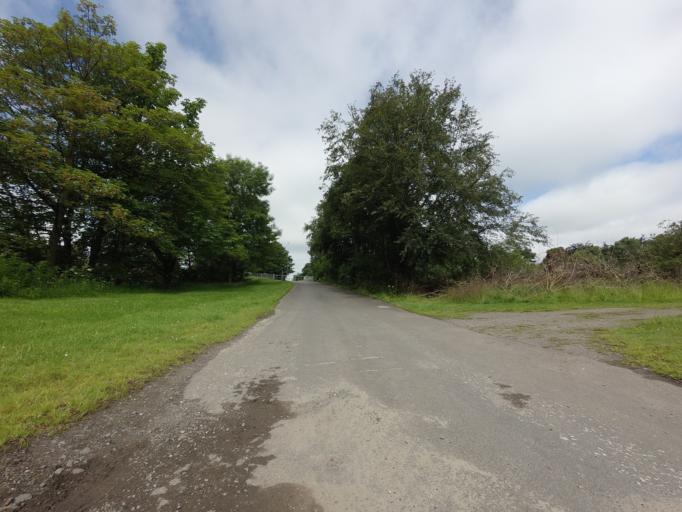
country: GB
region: Scotland
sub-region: Aberdeenshire
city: Turriff
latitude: 57.5337
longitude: -2.4609
